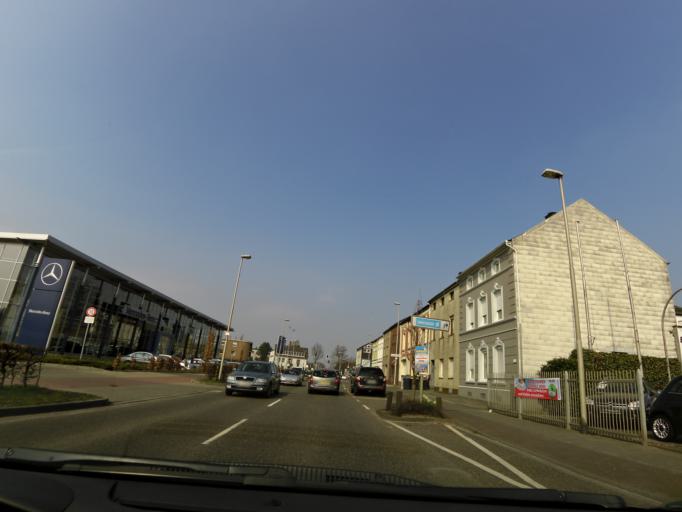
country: NL
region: Limburg
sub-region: Gemeente Kerkrade
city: Kerkrade
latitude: 50.8304
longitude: 6.0781
